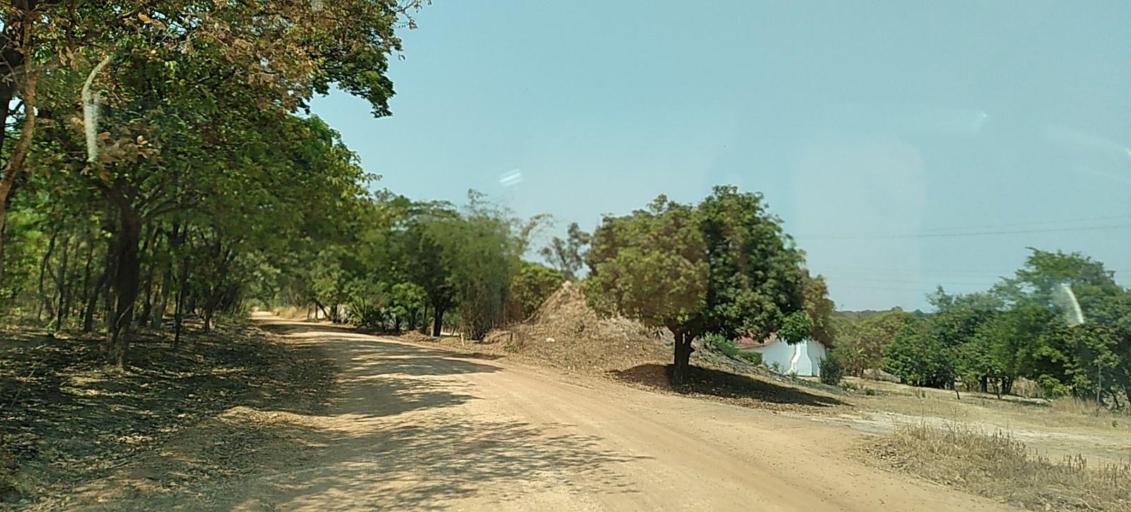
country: ZM
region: Copperbelt
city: Chambishi
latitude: -12.6070
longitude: 27.9597
